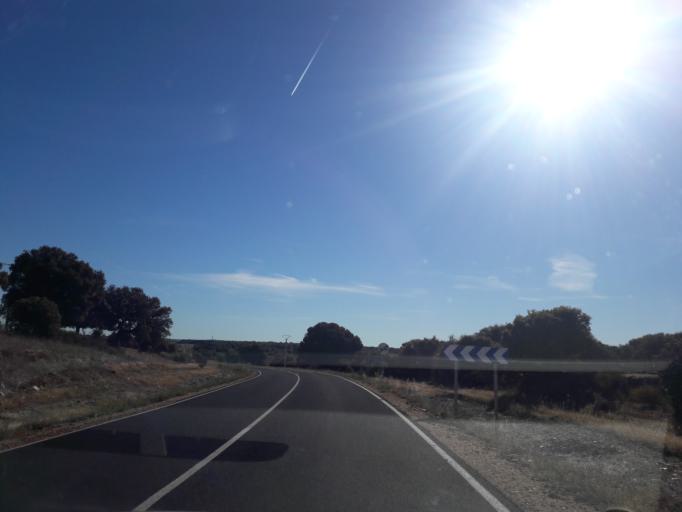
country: ES
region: Castille and Leon
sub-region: Provincia de Salamanca
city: Calzada de Don Diego
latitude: 40.8629
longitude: -5.8460
